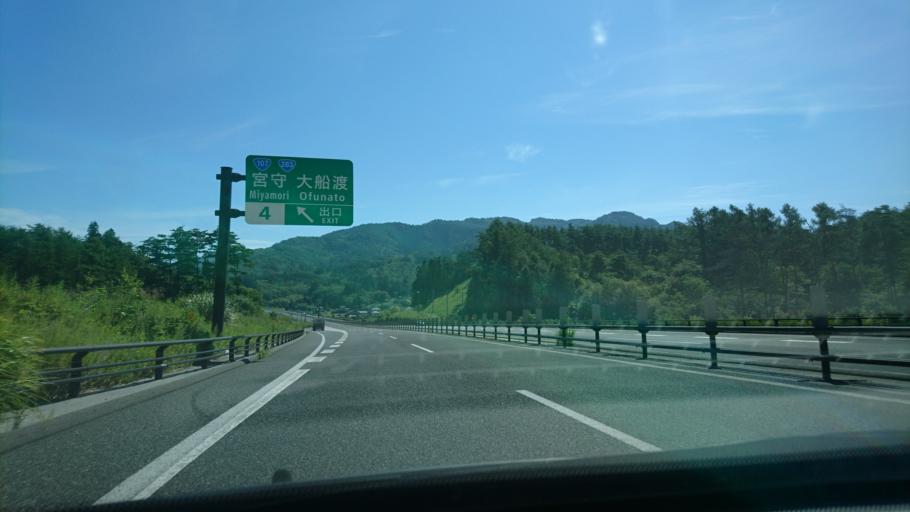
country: JP
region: Iwate
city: Tono
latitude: 39.2933
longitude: 141.3984
